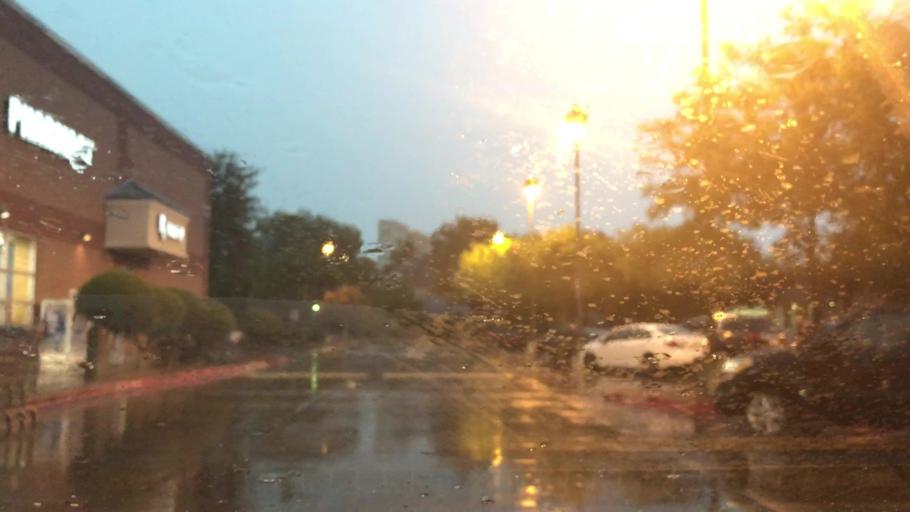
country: US
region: Texas
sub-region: Dallas County
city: Highland Park
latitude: 32.8131
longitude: -96.8125
